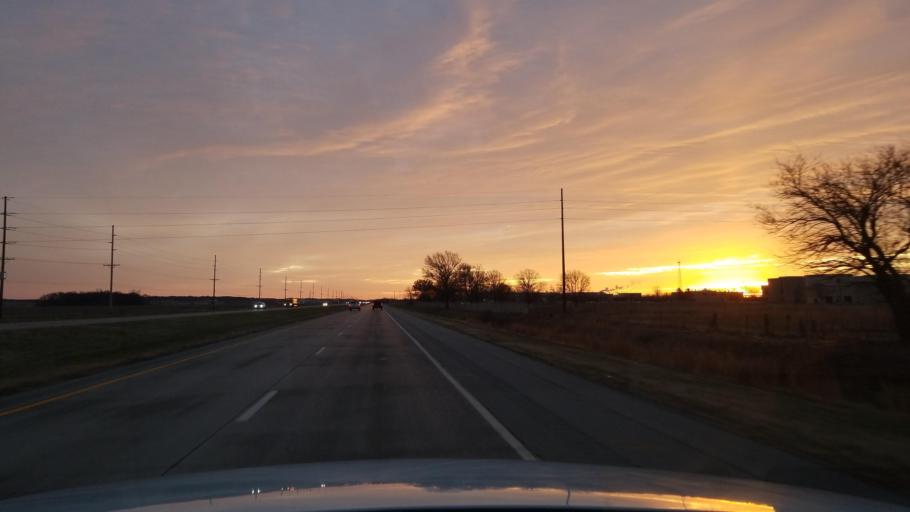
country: US
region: Indiana
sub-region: Posey County
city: Mount Vernon
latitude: 37.9427
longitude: -87.8467
